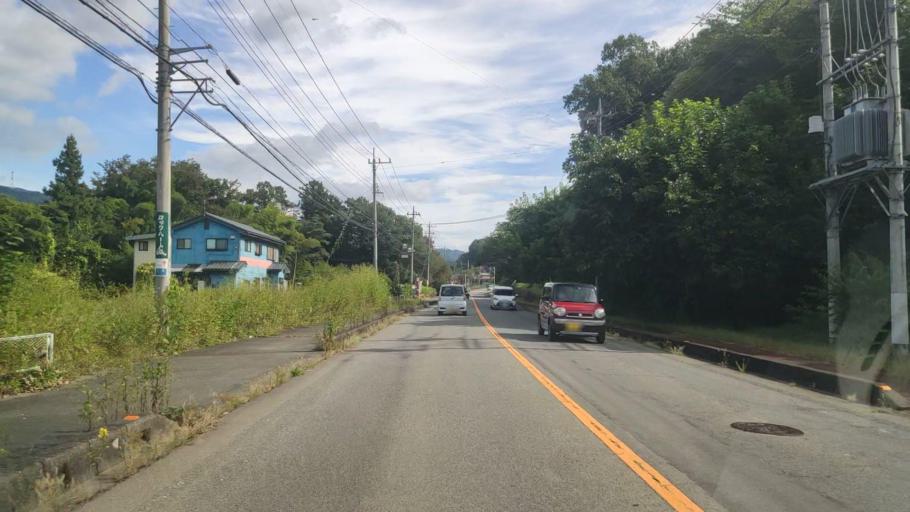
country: JP
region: Gunma
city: Nakanojomachi
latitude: 36.6092
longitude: 138.8803
